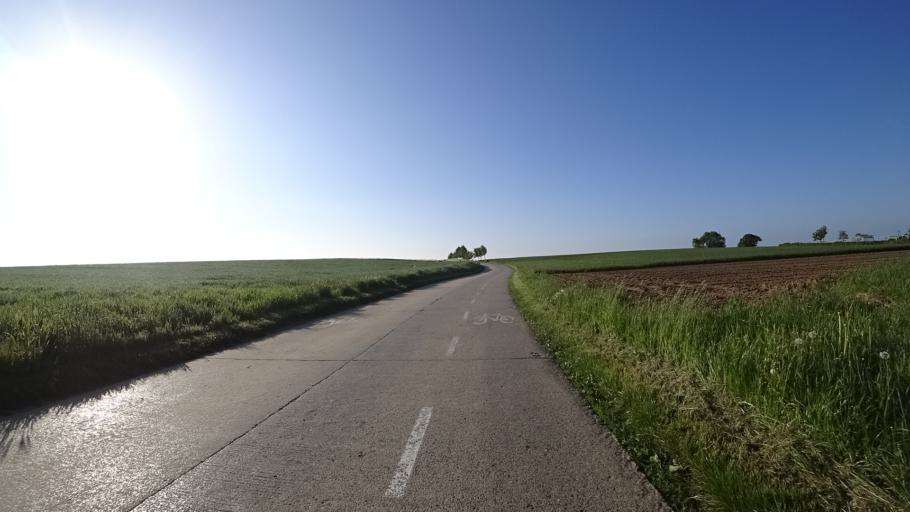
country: BE
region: Wallonia
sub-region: Province du Brabant Wallon
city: Walhain-Saint-Paul
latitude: 50.6364
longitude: 4.6774
